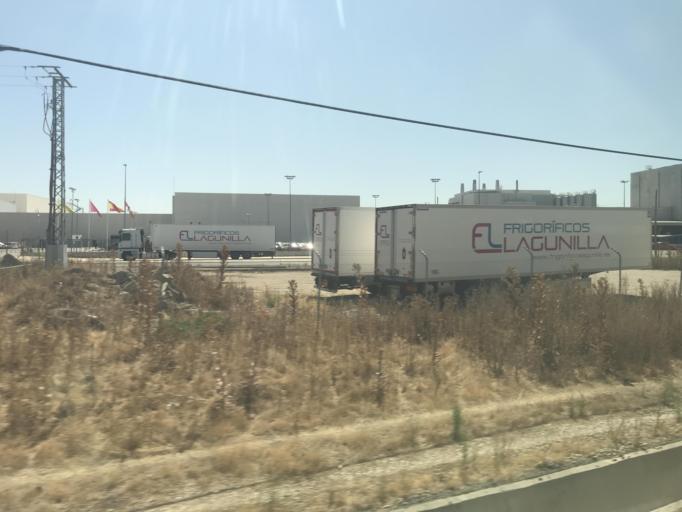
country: ES
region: Castille and Leon
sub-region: Provincia de Valladolid
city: Santovenia de Pisuerga
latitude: 41.6839
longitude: -4.6878
